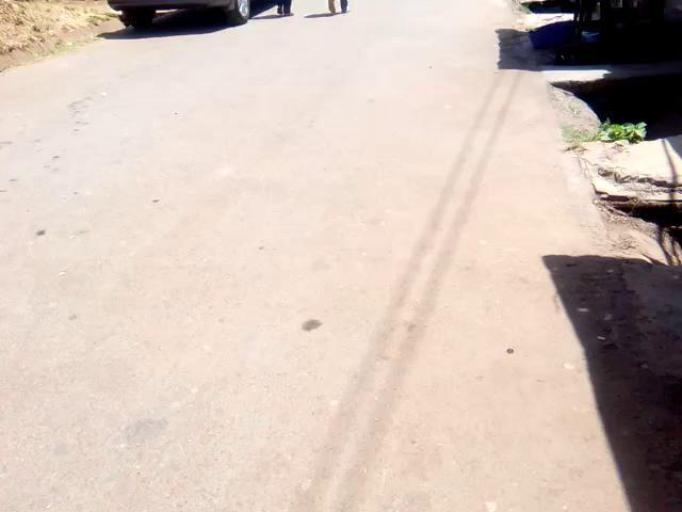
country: KE
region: Nairobi Area
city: Nairobi
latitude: -1.3168
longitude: 36.7750
